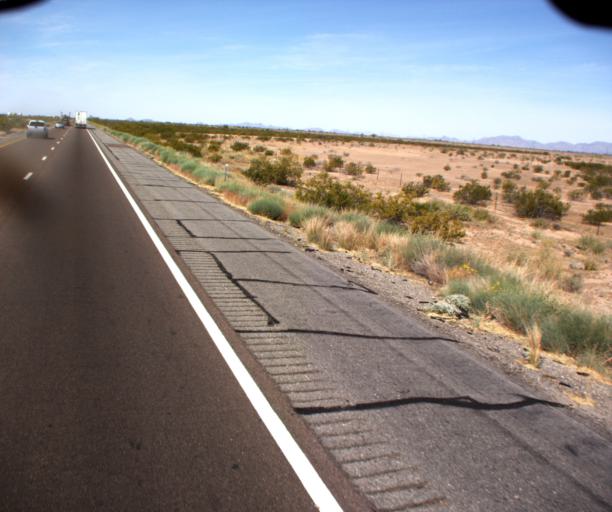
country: US
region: Arizona
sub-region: La Paz County
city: Salome
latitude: 33.5529
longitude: -113.2447
